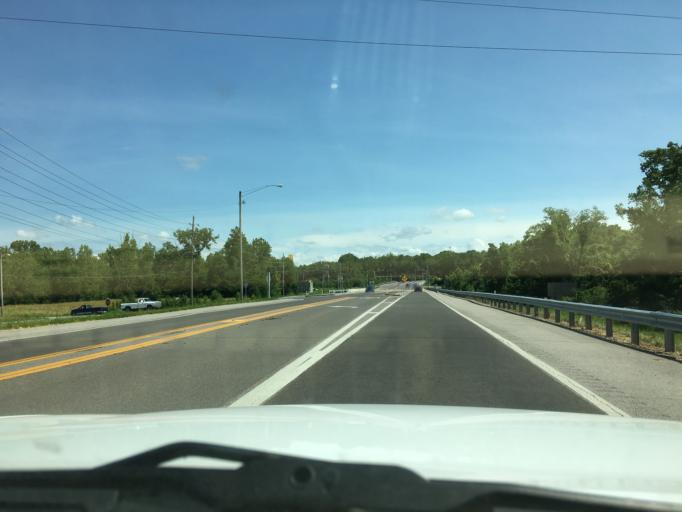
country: US
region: Missouri
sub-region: Franklin County
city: Union
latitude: 38.4486
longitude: -90.9996
